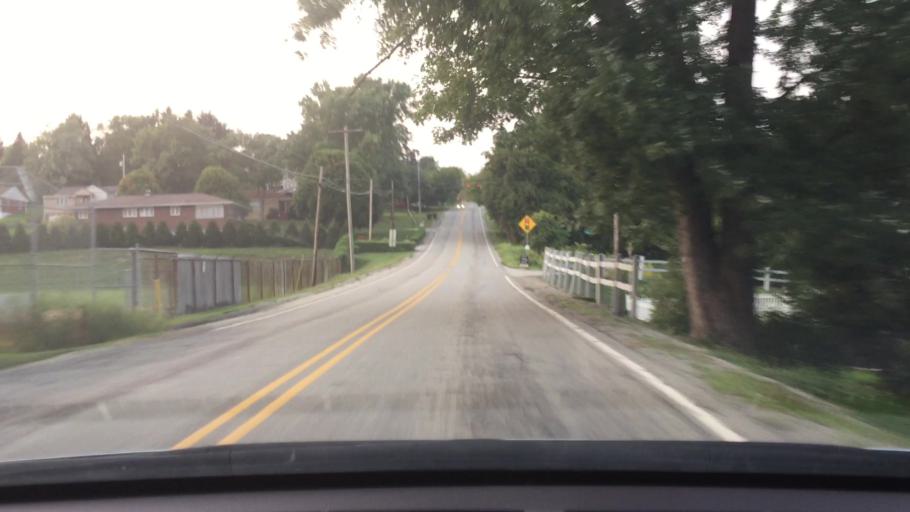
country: US
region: Pennsylvania
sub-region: Westmoreland County
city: Fellsburg
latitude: 40.1822
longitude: -79.8242
